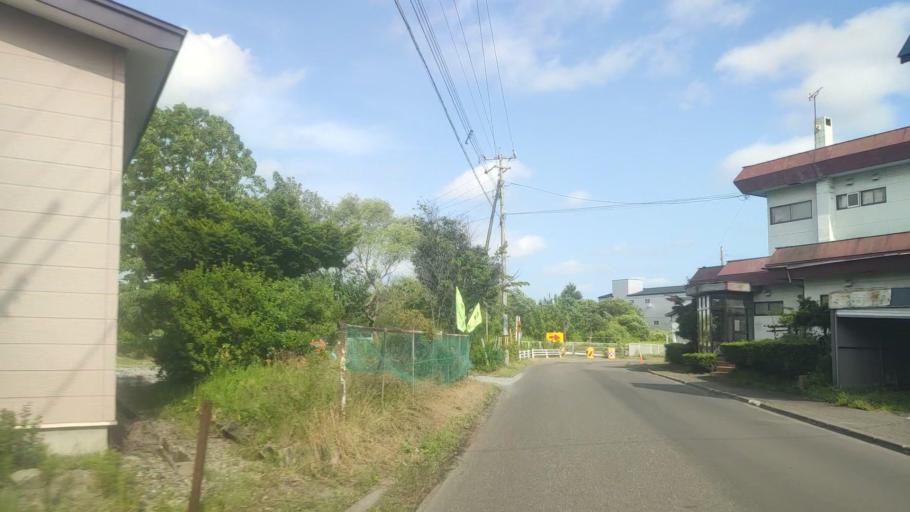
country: JP
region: Hokkaido
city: Tomakomai
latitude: 42.6490
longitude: 141.6284
